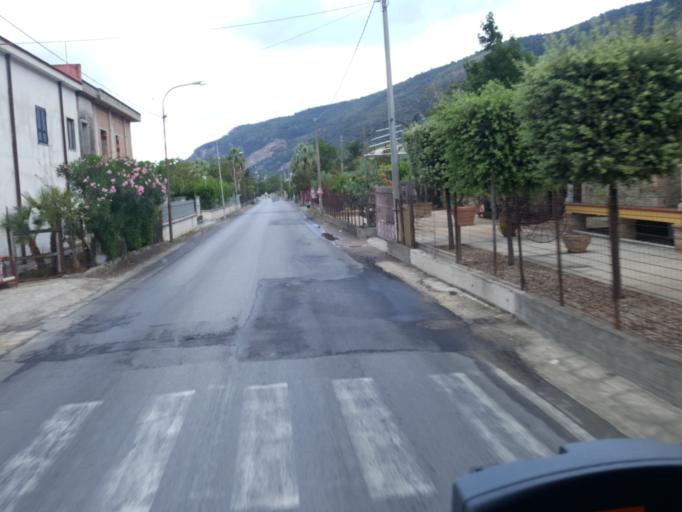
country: IT
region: Campania
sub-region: Provincia di Napoli
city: Striano
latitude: 40.8248
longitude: 14.5974
